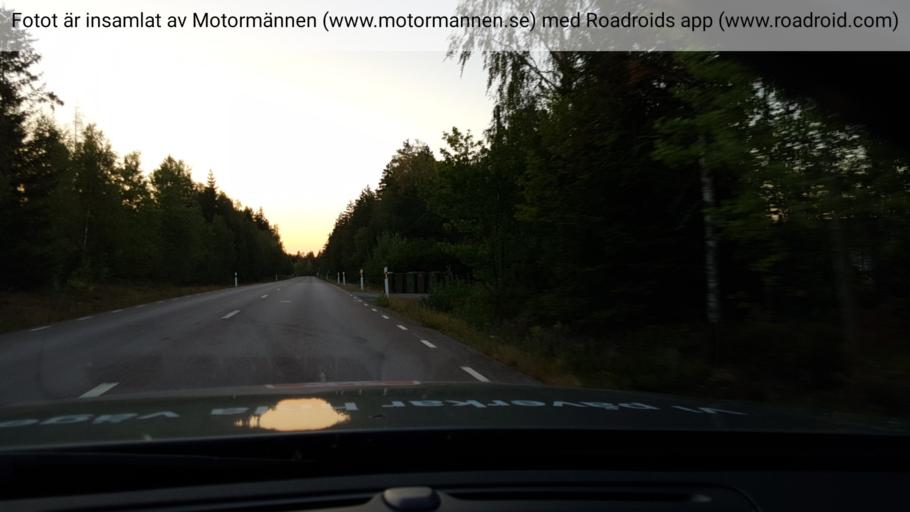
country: SE
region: Uppsala
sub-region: Heby Kommun
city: OEstervala
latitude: 60.0640
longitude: 17.2199
